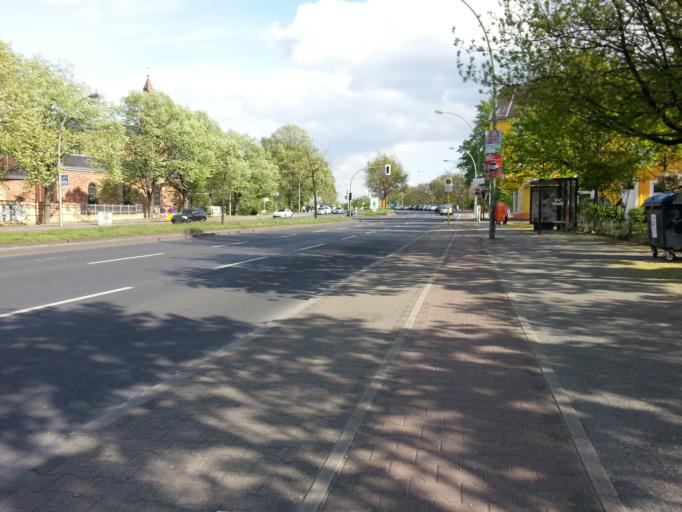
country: DE
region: Berlin
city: Spandau
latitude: 52.5391
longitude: 13.2064
